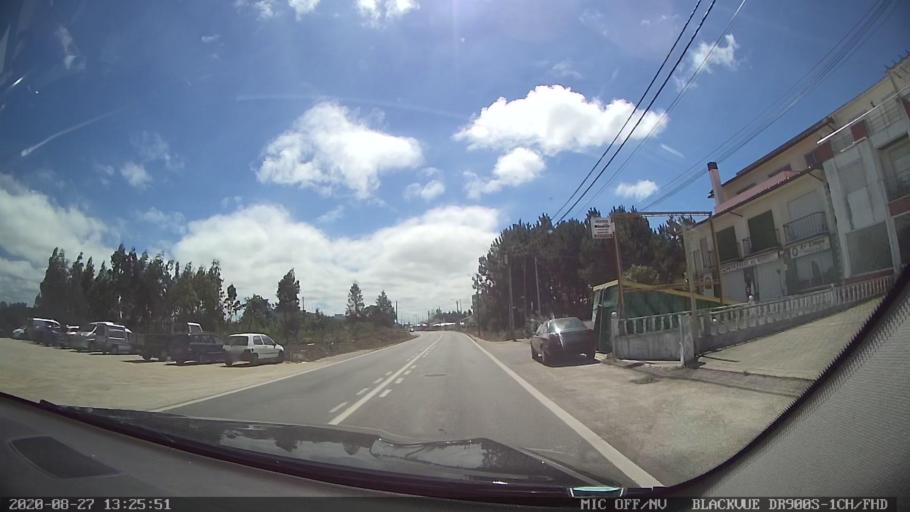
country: PT
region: Aveiro
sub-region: Vagos
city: Vagos
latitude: 40.5426
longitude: -8.6780
